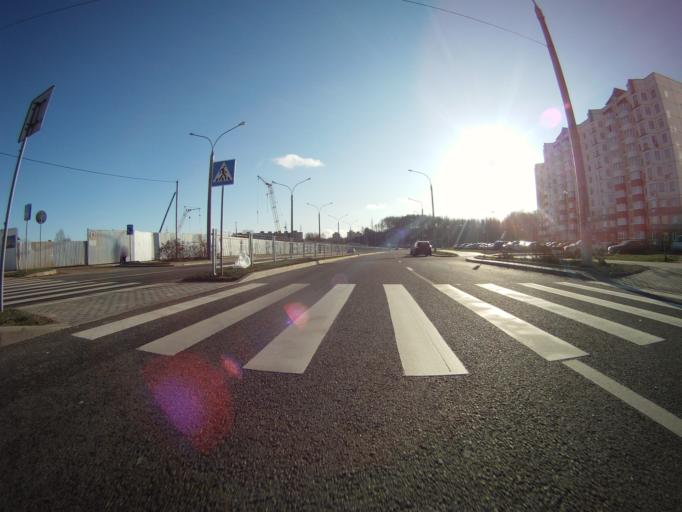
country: BY
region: Minsk
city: Novoye Medvezhino
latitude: 53.8749
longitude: 27.4553
